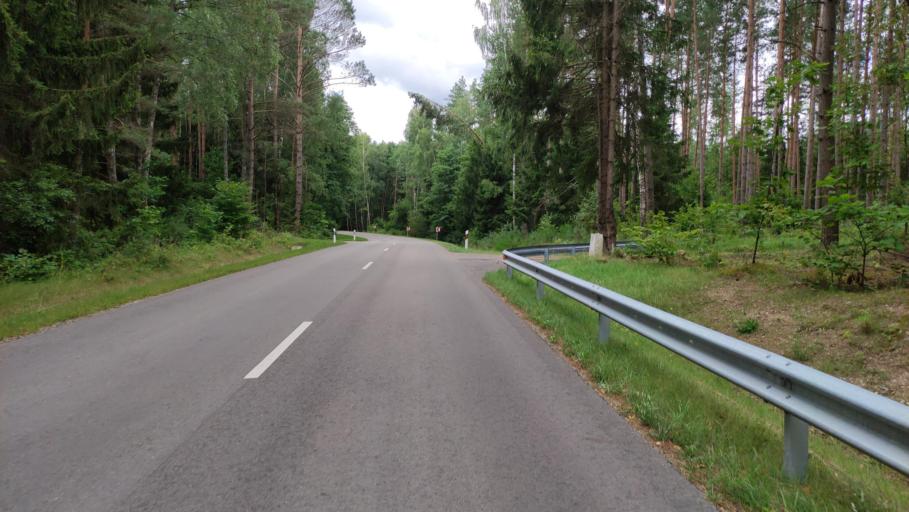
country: LT
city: Veisiejai
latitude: 54.1461
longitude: 23.7057
